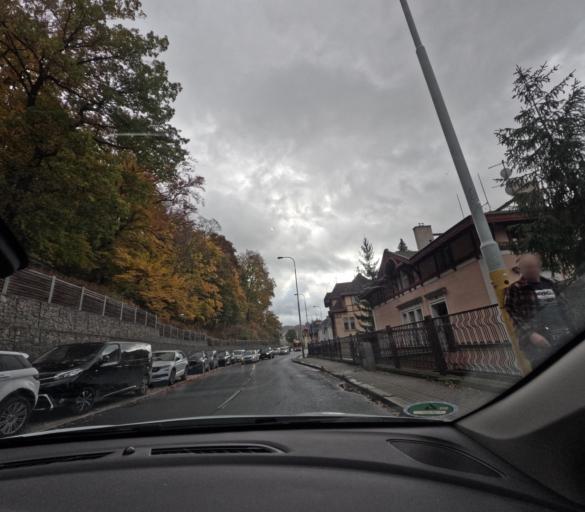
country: CZ
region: Karlovarsky
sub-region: Okres Karlovy Vary
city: Karlovy Vary
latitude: 50.2276
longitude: 12.8825
